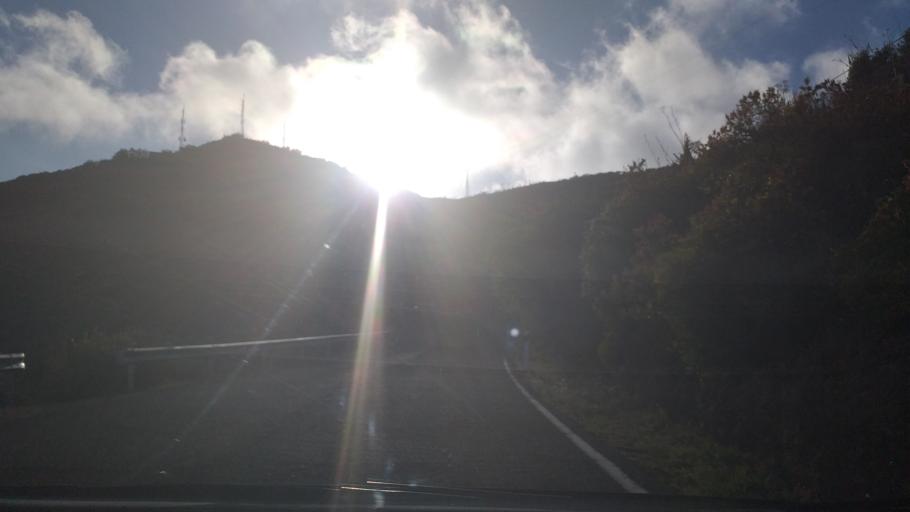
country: ES
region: Canary Islands
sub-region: Provincia de Las Palmas
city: Valsequillo de Gran Canaria
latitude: 27.9585
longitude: -15.5012
